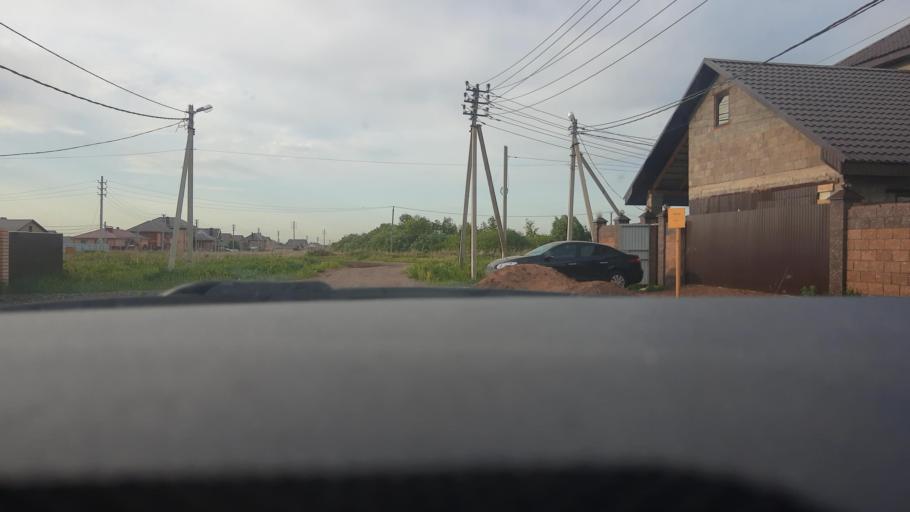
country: RU
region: Bashkortostan
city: Kabakovo
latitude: 54.6059
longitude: 56.1225
